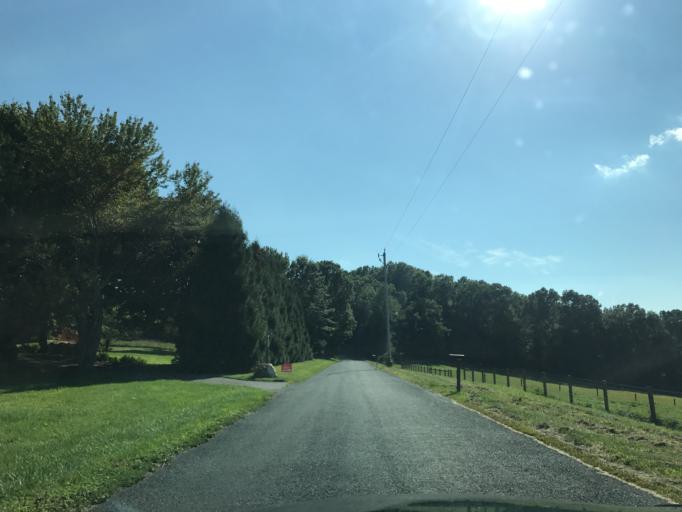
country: US
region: Pennsylvania
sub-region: York County
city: Stewartstown
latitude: 39.7035
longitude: -76.5555
